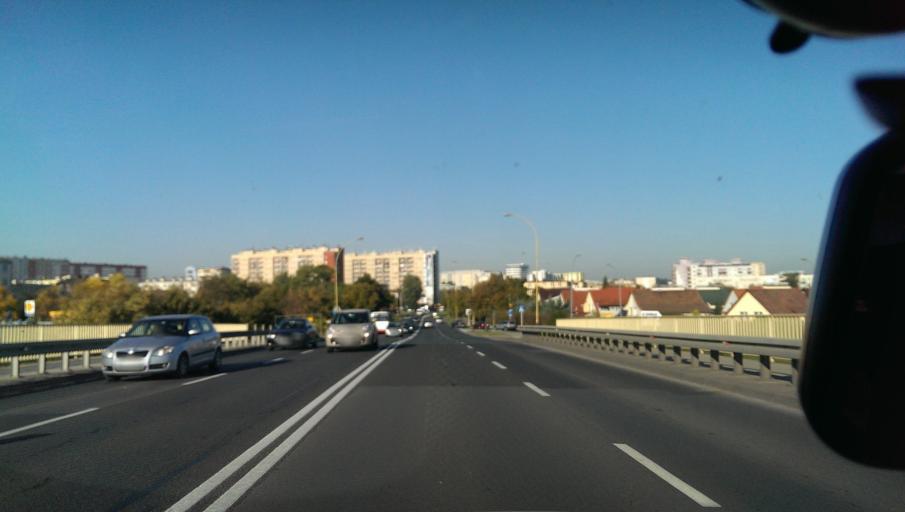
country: PL
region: Subcarpathian Voivodeship
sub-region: Rzeszow
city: Rzeszow
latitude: 50.0431
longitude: 21.9917
